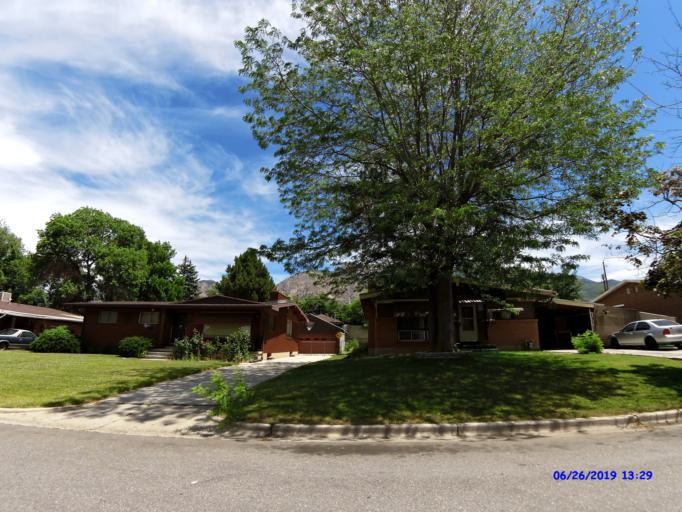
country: US
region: Utah
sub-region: Weber County
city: South Ogden
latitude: 41.2022
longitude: -111.9581
